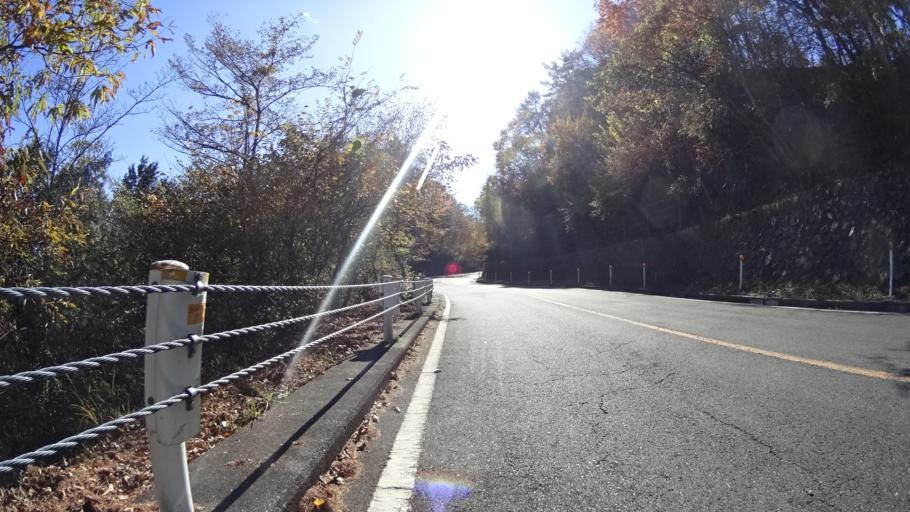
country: JP
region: Yamanashi
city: Uenohara
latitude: 35.7515
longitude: 139.0404
